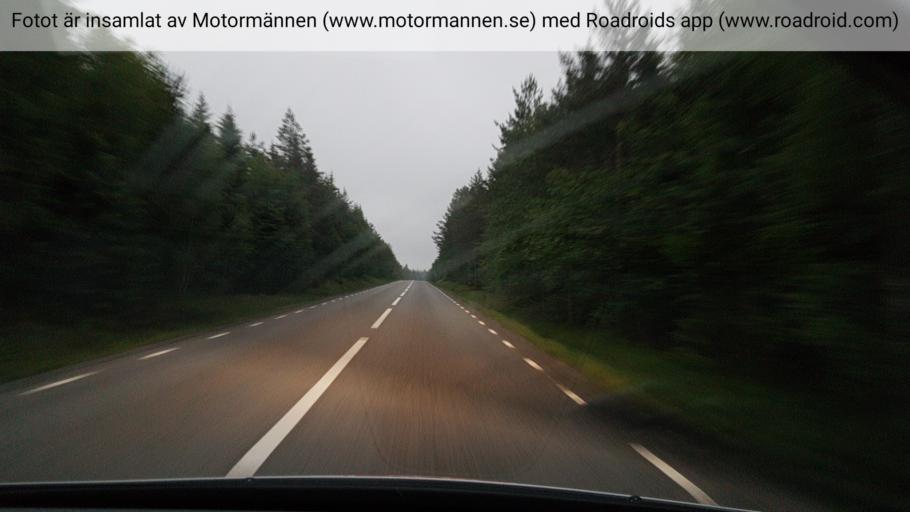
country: SE
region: OErebro
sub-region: Lindesbergs Kommun
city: Stora
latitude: 59.9015
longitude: 15.2025
